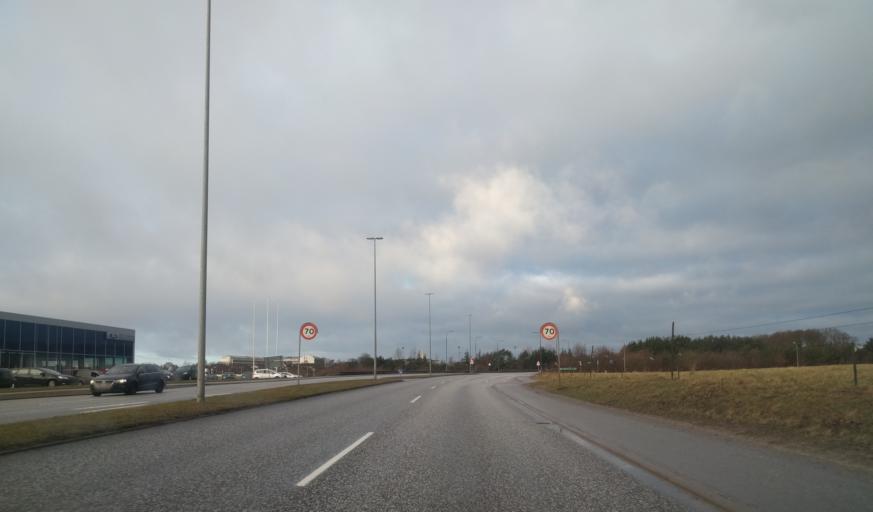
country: DK
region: North Denmark
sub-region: Alborg Kommune
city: Gistrup
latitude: 57.0305
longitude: 9.9763
